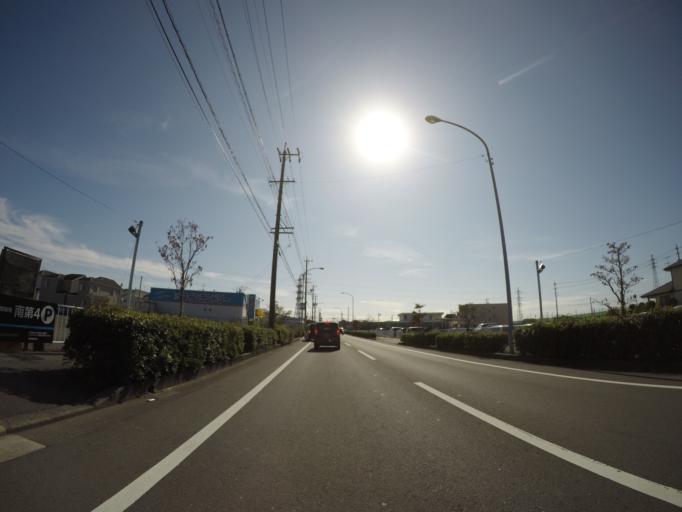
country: JP
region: Shizuoka
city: Shizuoka-shi
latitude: 34.9691
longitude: 138.4209
